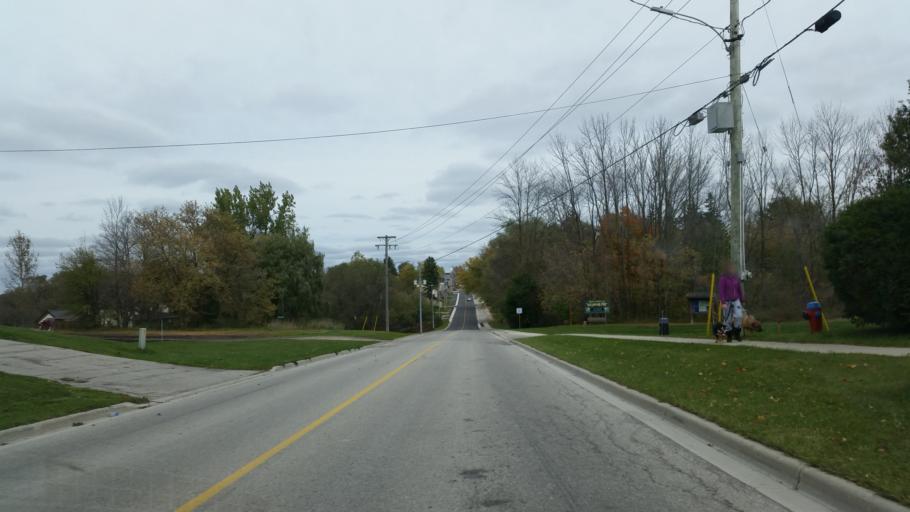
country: CA
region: Ontario
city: Hanover
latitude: 44.0386
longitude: -81.1228
